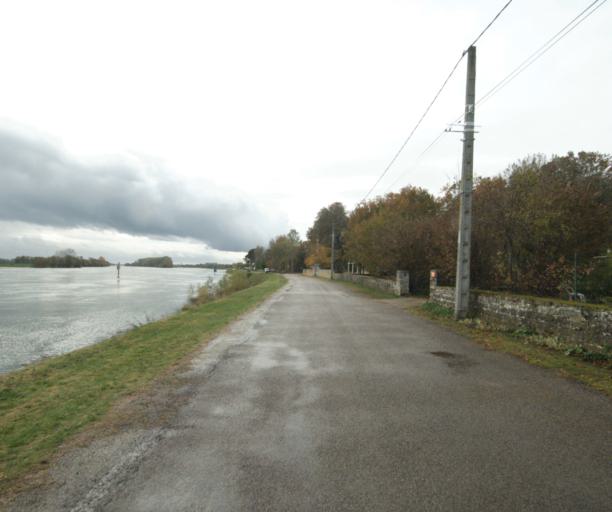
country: FR
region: Rhone-Alpes
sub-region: Departement de l'Ain
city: Pont-de-Vaux
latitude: 46.4468
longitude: 4.8935
